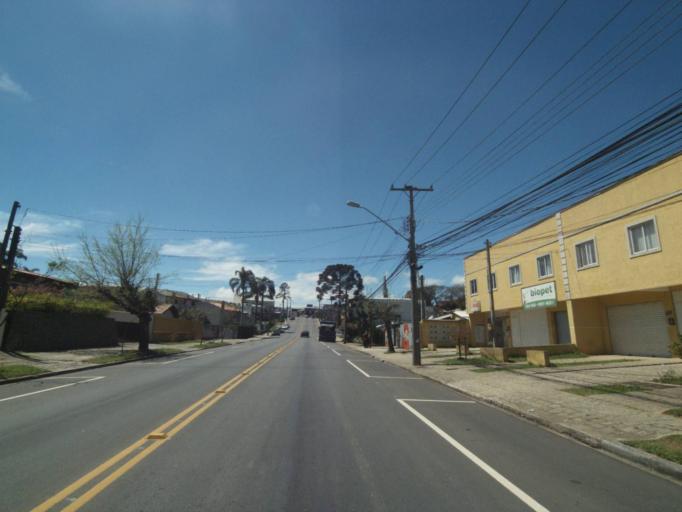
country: BR
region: Parana
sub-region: Curitiba
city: Curitiba
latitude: -25.3895
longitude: -49.2628
